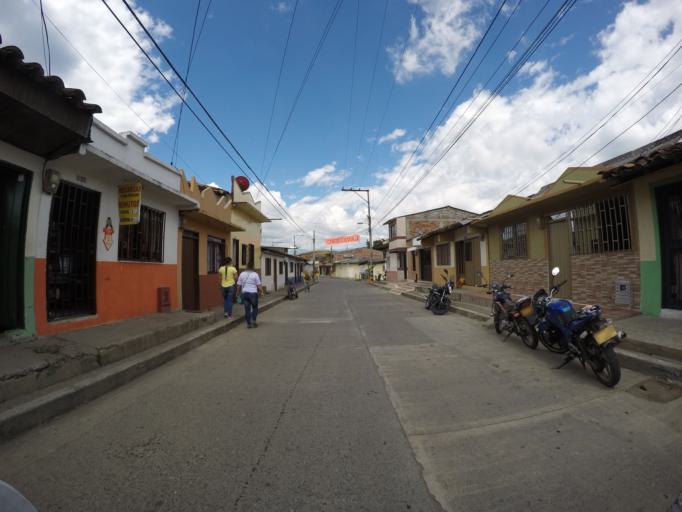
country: CO
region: Valle del Cauca
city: Alcala
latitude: 4.6755
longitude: -75.7858
